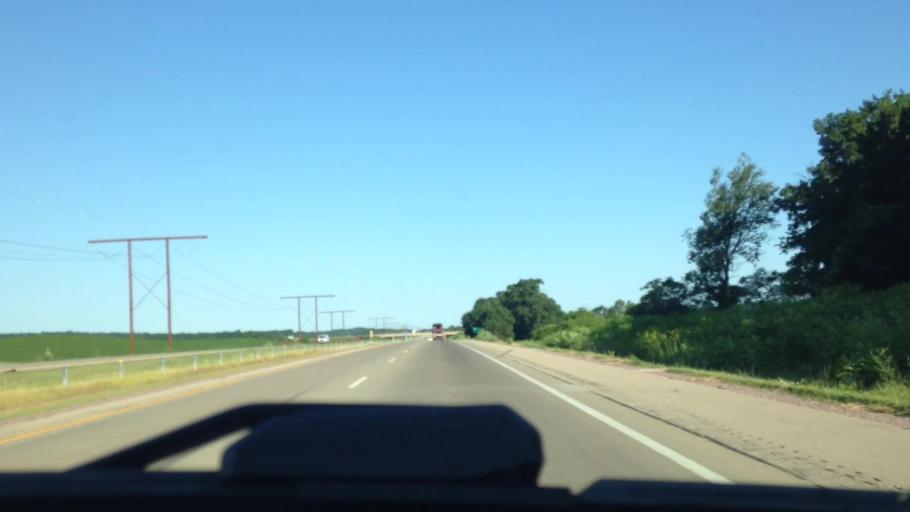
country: US
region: Wisconsin
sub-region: Sauk County
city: Baraboo
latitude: 43.5573
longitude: -89.7096
